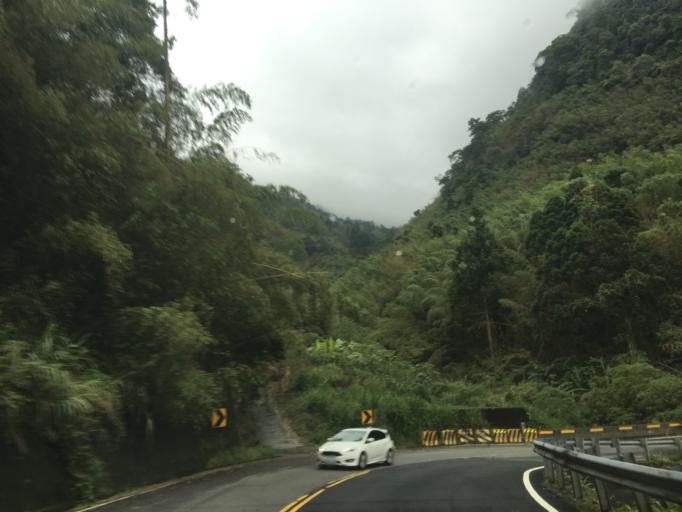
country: TW
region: Taiwan
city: Lugu
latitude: 23.4979
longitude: 120.7025
